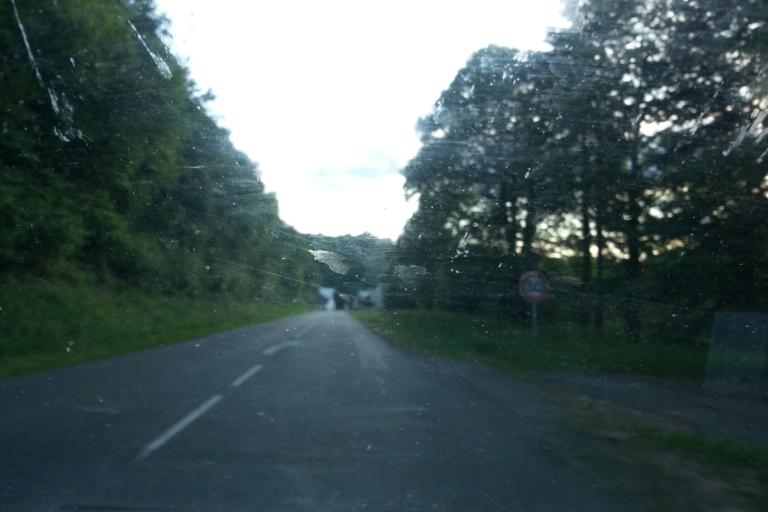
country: FR
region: Brittany
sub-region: Departement du Morbihan
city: Guemene-sur-Scorff
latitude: 48.0724
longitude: -3.2064
